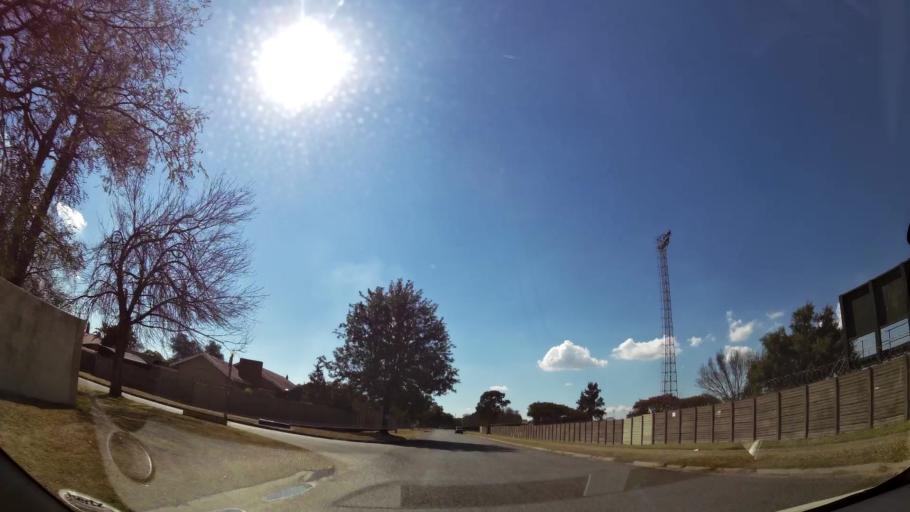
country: ZA
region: Mpumalanga
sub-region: Nkangala District Municipality
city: Witbank
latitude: -25.8844
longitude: 29.2251
